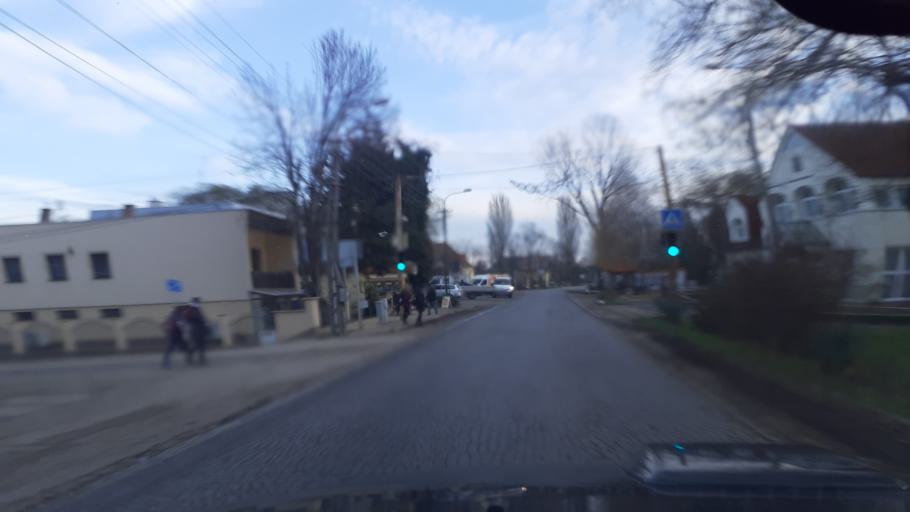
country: HU
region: Bacs-Kiskun
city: Kunszentmiklos
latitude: 47.0260
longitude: 19.1243
